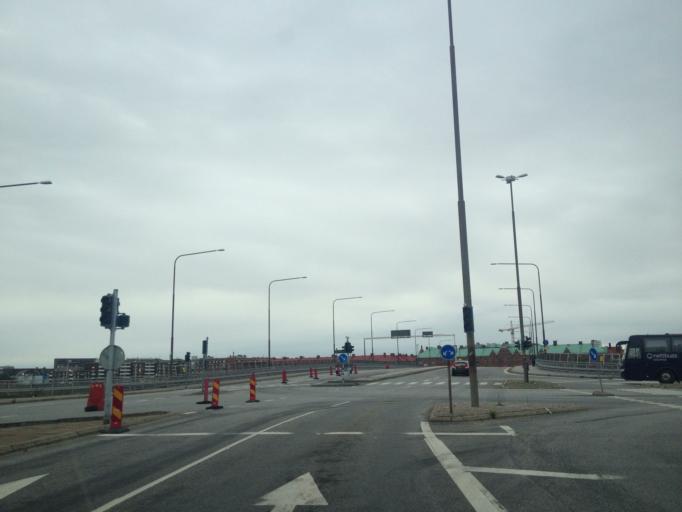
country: SE
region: Skane
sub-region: Malmo
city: Malmoe
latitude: 55.6124
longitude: 13.0182
